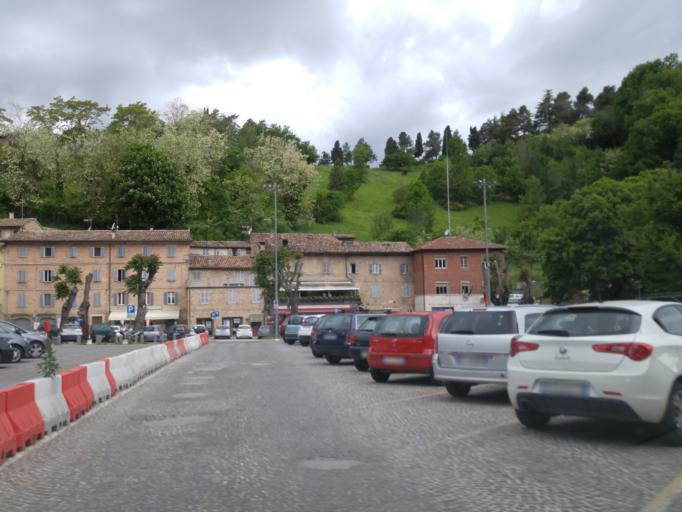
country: IT
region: The Marches
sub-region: Provincia di Pesaro e Urbino
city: Urbino
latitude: 43.7240
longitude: 12.6351
